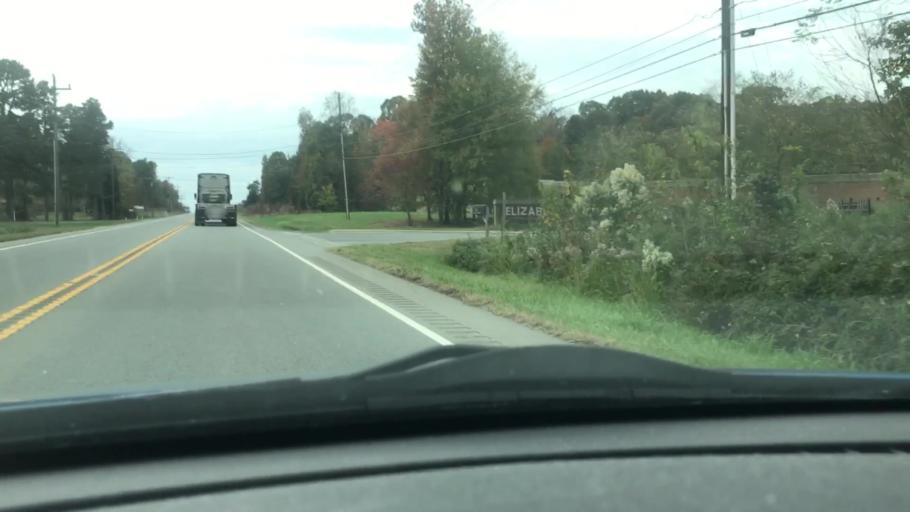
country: US
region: North Carolina
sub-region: Davidson County
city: Thomasville
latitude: 35.7943
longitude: -80.1453
